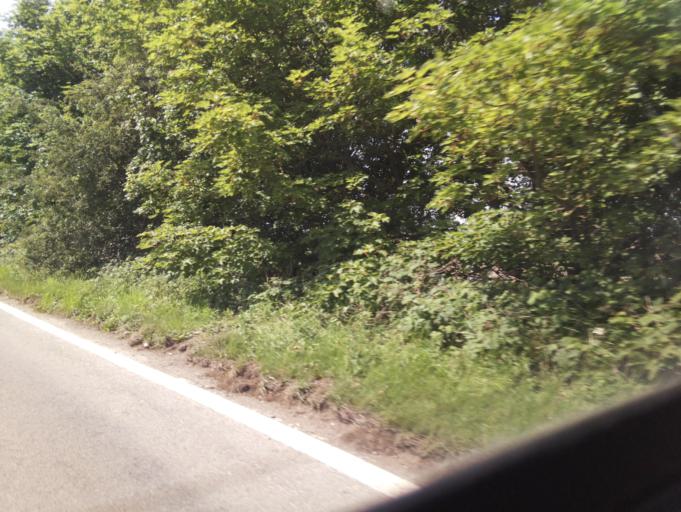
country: GB
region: England
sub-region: North Lincolnshire
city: Manton
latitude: 53.5108
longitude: -0.5818
